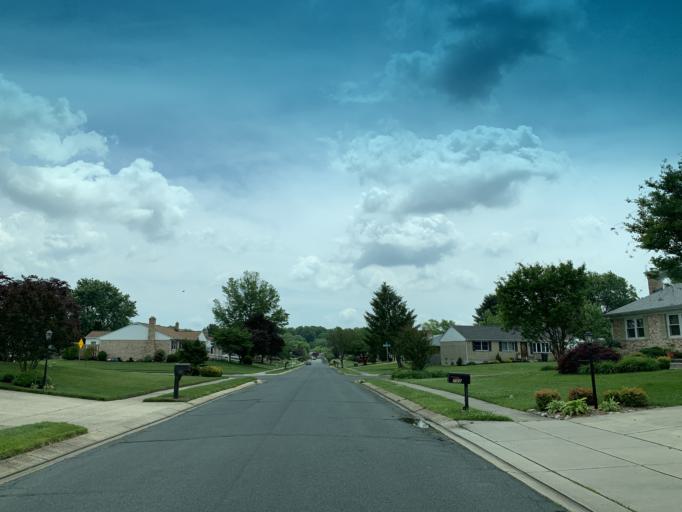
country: US
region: Maryland
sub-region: Harford County
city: South Bel Air
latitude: 39.5402
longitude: -76.2994
